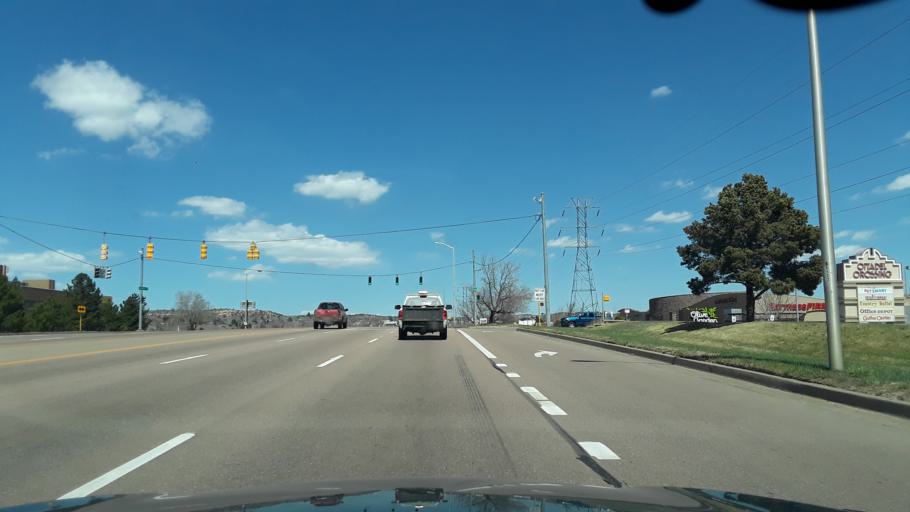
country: US
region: Colorado
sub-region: El Paso County
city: Cimarron Hills
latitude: 38.8414
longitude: -104.7572
